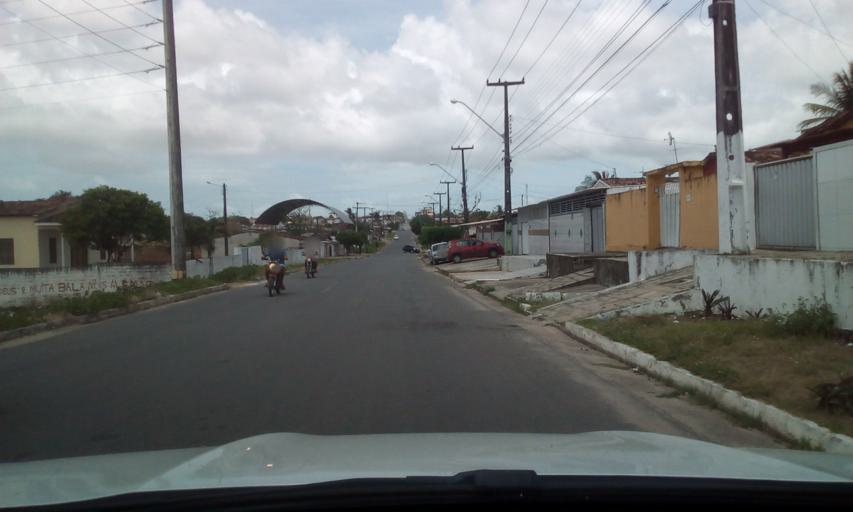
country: BR
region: Paraiba
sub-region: Bayeux
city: Bayeux
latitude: -7.1784
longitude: -34.8903
